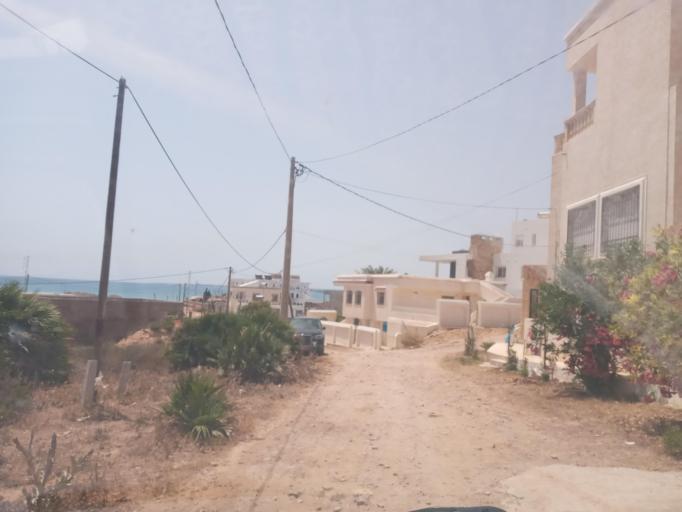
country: TN
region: Nabul
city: El Haouaria
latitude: 37.0430
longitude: 11.0615
